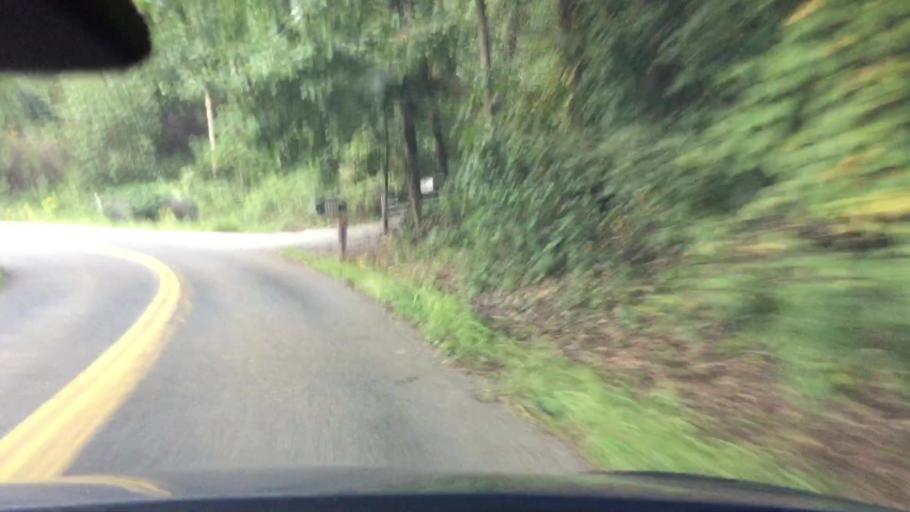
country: US
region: Pennsylvania
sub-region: Allegheny County
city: Bakerstown
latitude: 40.6416
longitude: -79.8978
